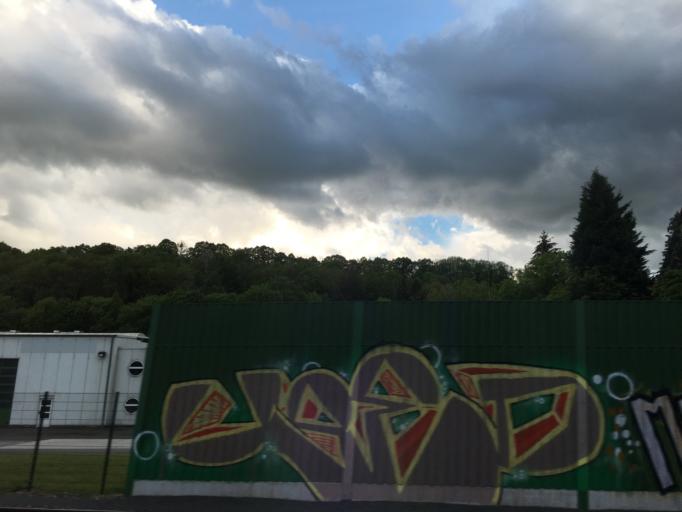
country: DE
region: Saxony
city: Heidenau
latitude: 50.9607
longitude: 13.8948
